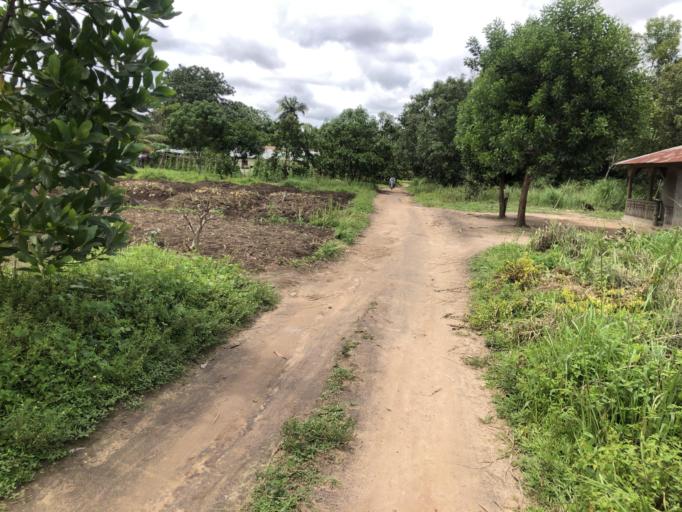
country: SL
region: Northern Province
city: Lunsar
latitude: 8.7136
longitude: -12.5169
